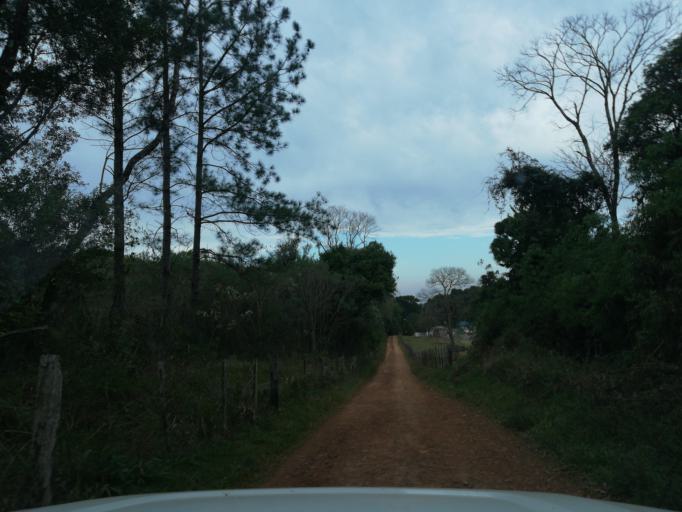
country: AR
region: Misiones
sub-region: Departamento de San Pedro
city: San Pedro
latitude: -26.6350
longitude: -54.1001
